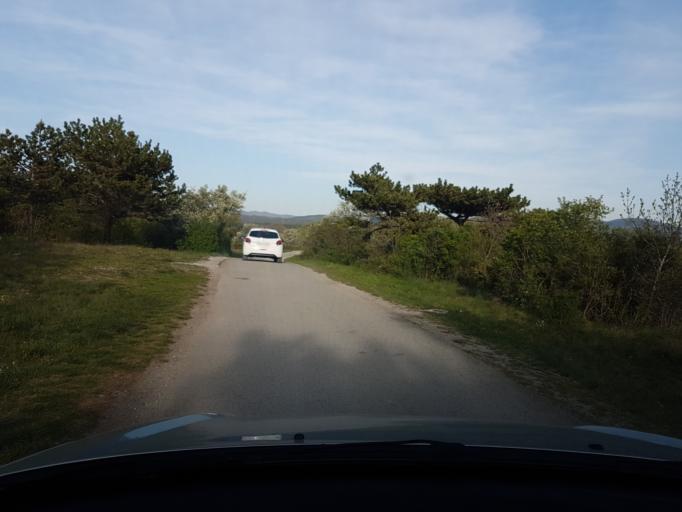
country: IT
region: Friuli Venezia Giulia
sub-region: Provincia di Trieste
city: Dolina
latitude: 45.5891
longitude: 13.8645
